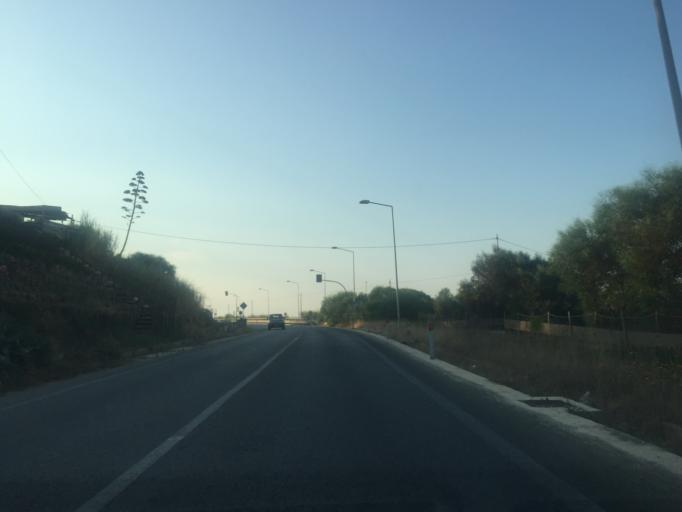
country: IT
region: Sicily
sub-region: Ragusa
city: Cava d'Aliga
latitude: 36.7158
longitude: 14.7582
